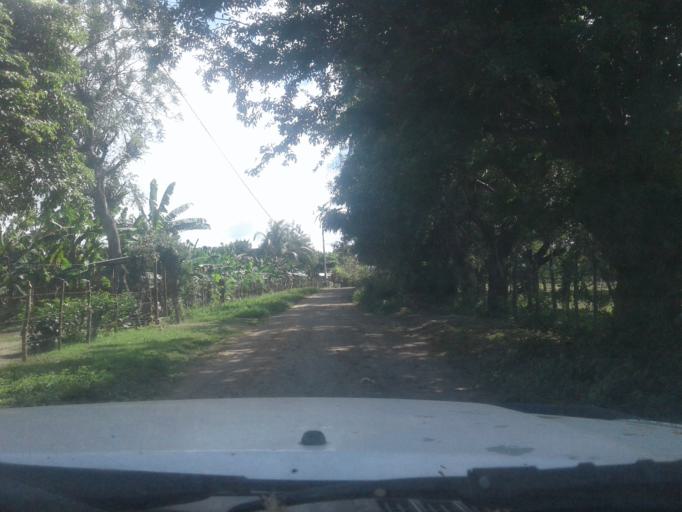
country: NI
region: Rivas
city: Buenos Aires
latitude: 11.5122
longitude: -85.8026
